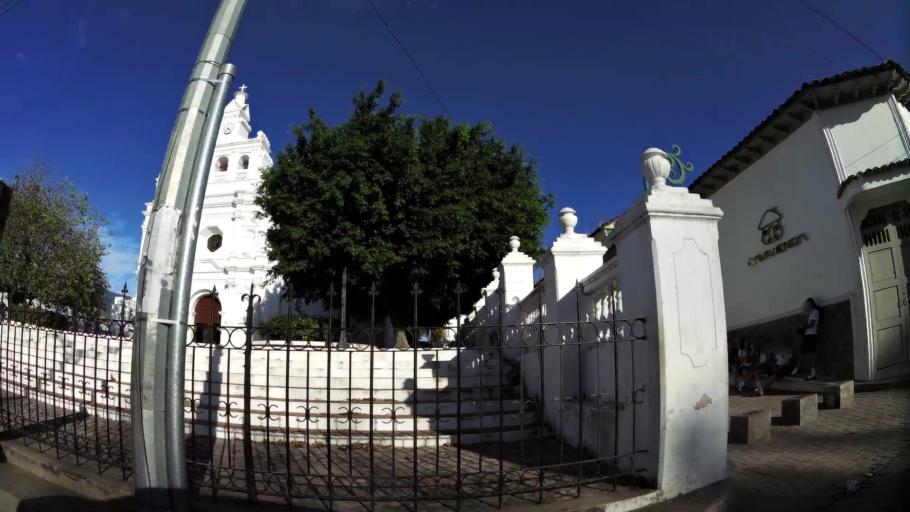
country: SV
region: Santa Ana
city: Metapan
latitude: 14.3318
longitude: -89.4477
